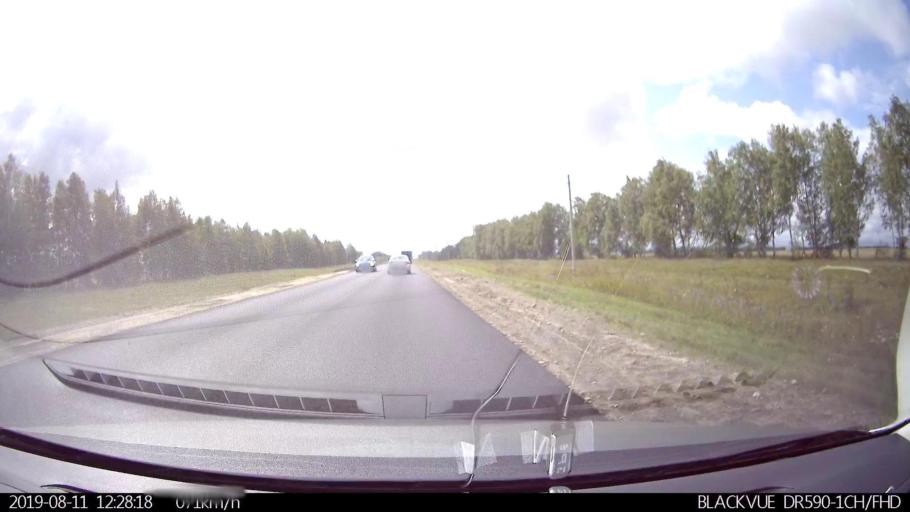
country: RU
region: Ulyanovsk
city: Ignatovka
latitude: 53.8452
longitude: 47.9121
